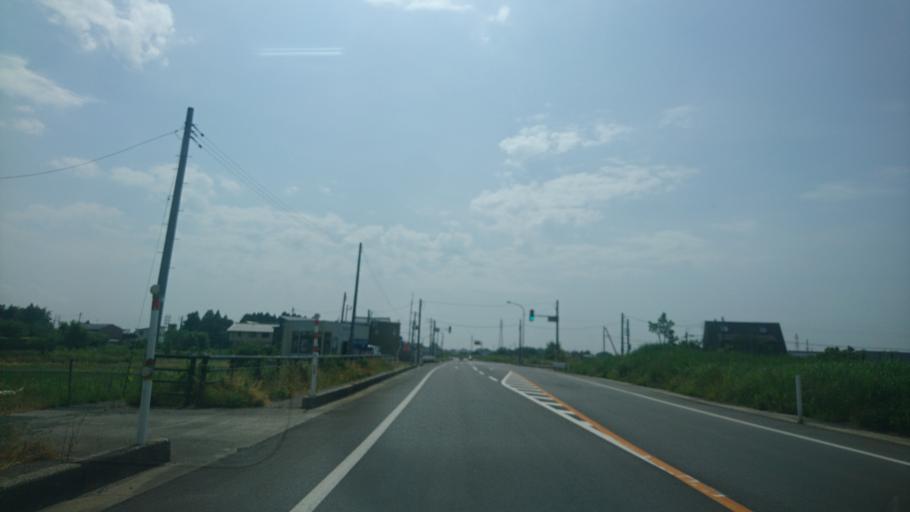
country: JP
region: Niigata
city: Shibata
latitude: 38.0621
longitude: 139.4219
